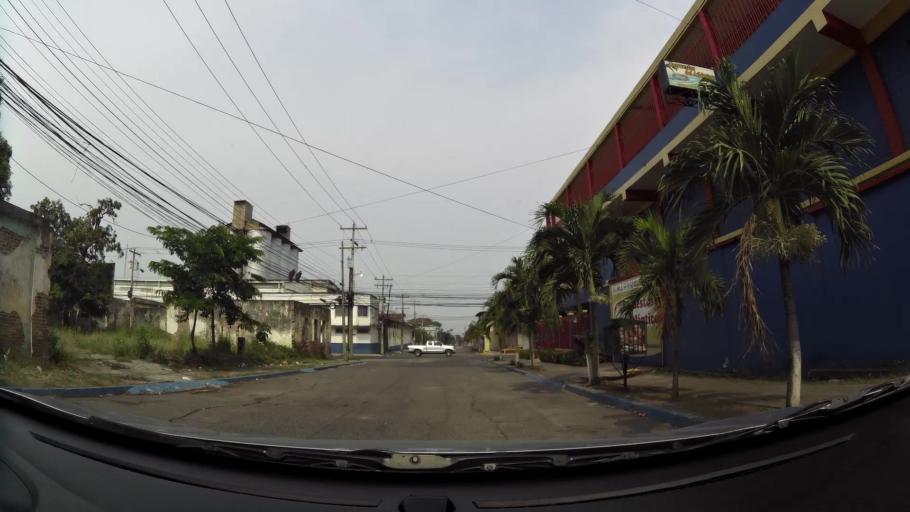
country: HN
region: Cortes
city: San Pedro Sula
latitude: 15.4929
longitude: -88.0263
